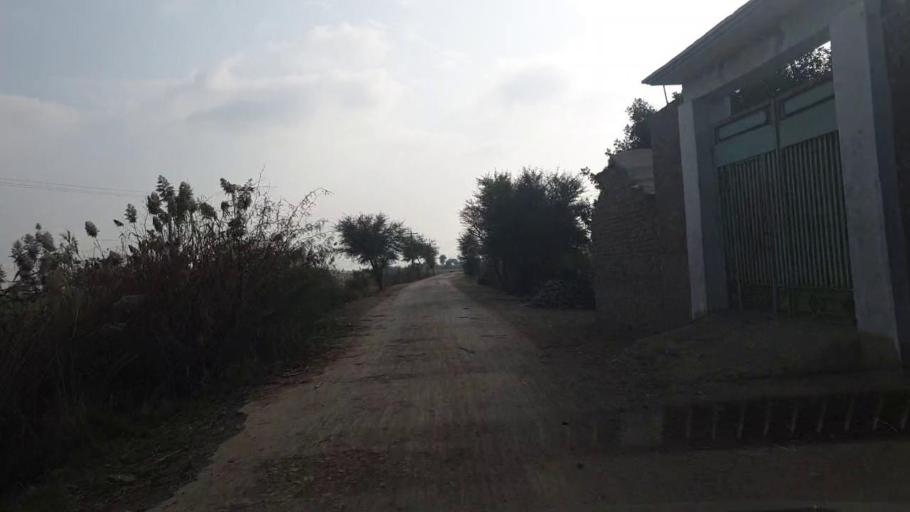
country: PK
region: Sindh
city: Shahdadpur
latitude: 25.8785
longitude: 68.6662
